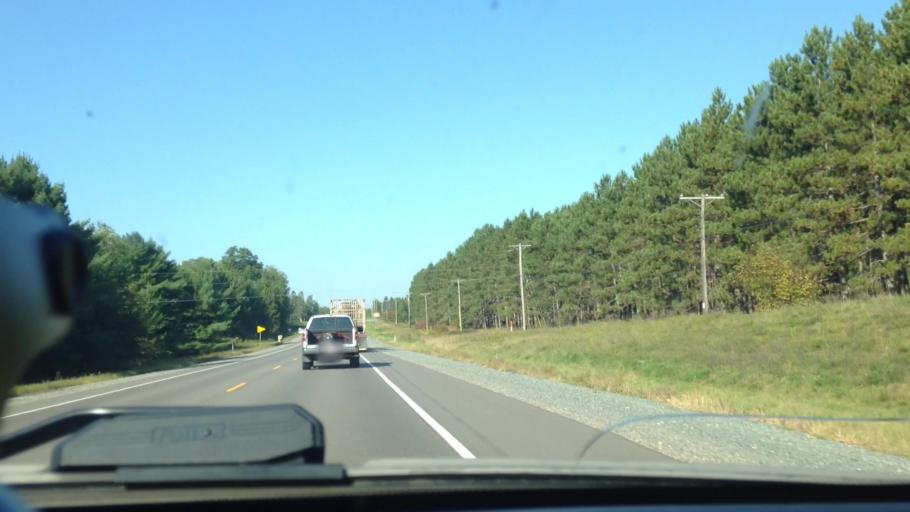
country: US
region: Michigan
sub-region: Dickinson County
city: Iron Mountain
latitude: 45.8760
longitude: -88.1019
